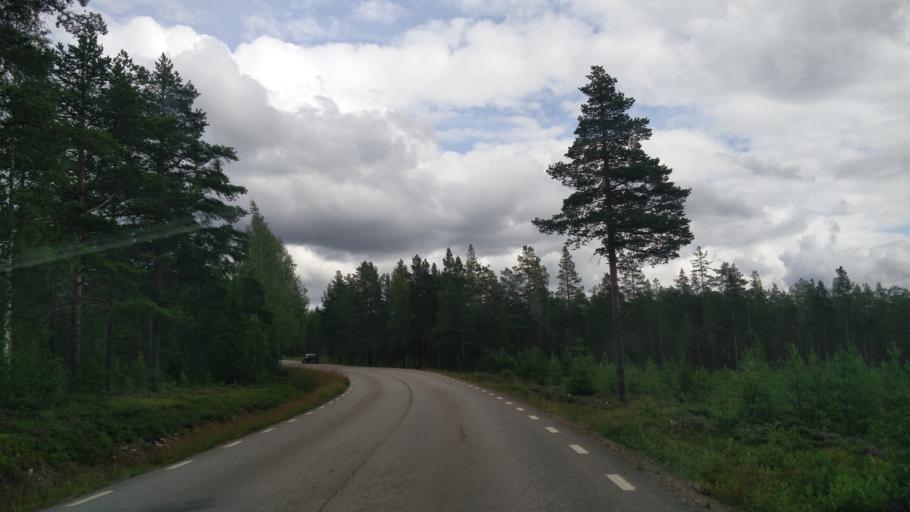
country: NO
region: Hedmark
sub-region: Trysil
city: Innbygda
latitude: 61.1767
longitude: 12.8560
